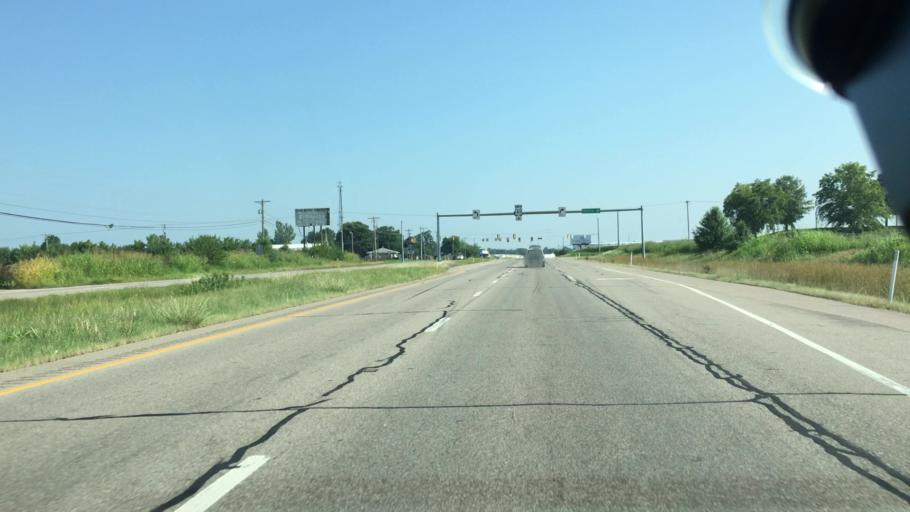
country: US
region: Indiana
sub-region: Gibson County
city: Fort Branch
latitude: 38.3021
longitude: -87.5673
